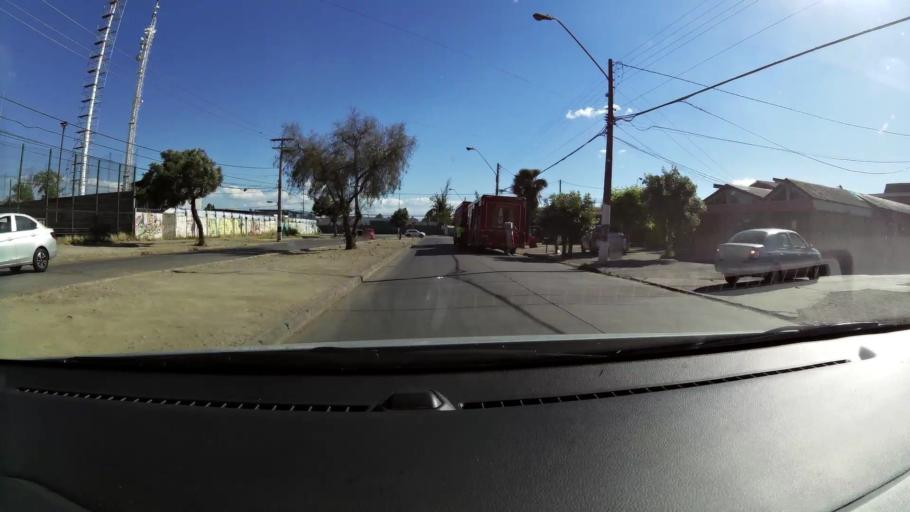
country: CL
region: Santiago Metropolitan
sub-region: Provincia de Maipo
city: San Bernardo
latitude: -33.5448
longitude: -70.7737
